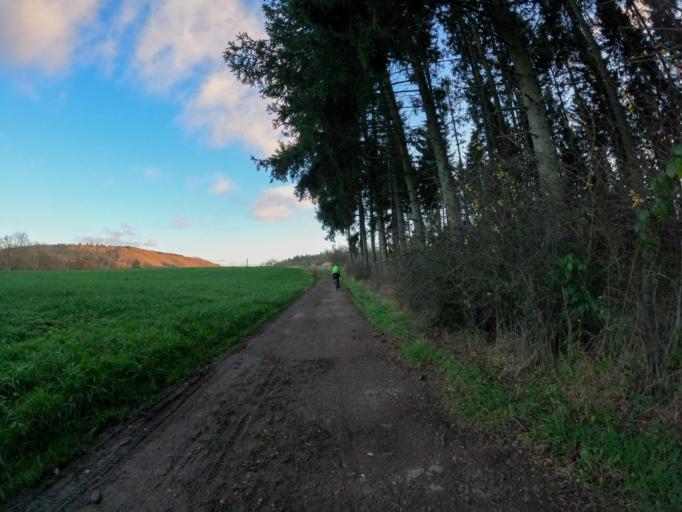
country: LU
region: Diekirch
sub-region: Canton de Wiltz
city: Bavigne
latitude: 49.9166
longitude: 5.8538
